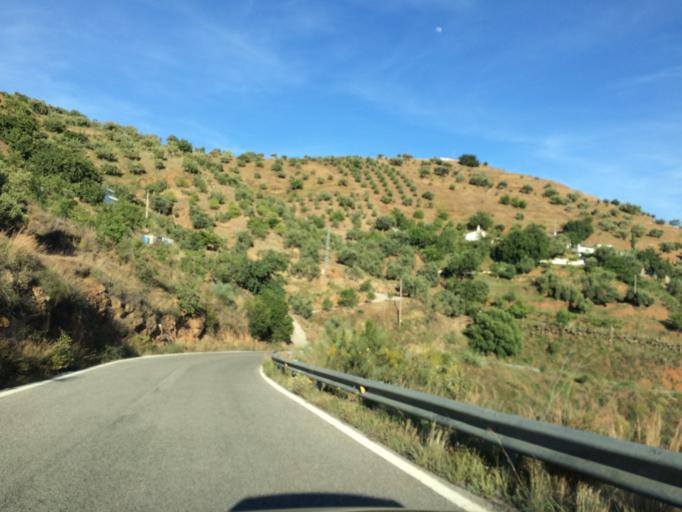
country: ES
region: Andalusia
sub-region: Provincia de Malaga
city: Totalan
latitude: 36.7481
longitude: -4.3314
